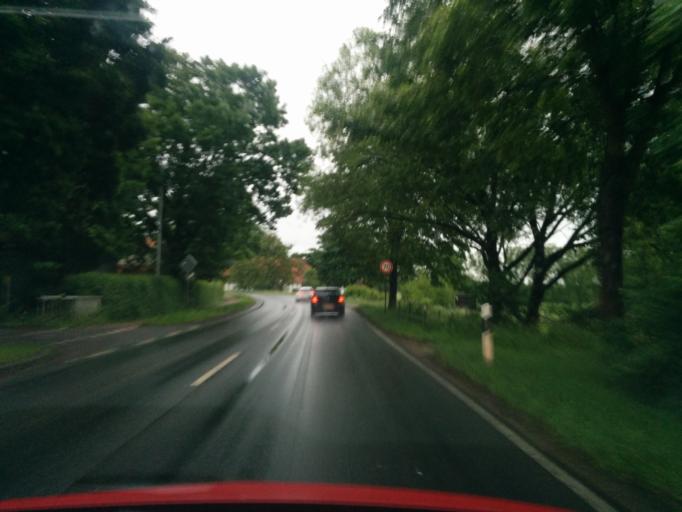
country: DE
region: Lower Saxony
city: Gieboldehausen
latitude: 51.6144
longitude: 10.2260
